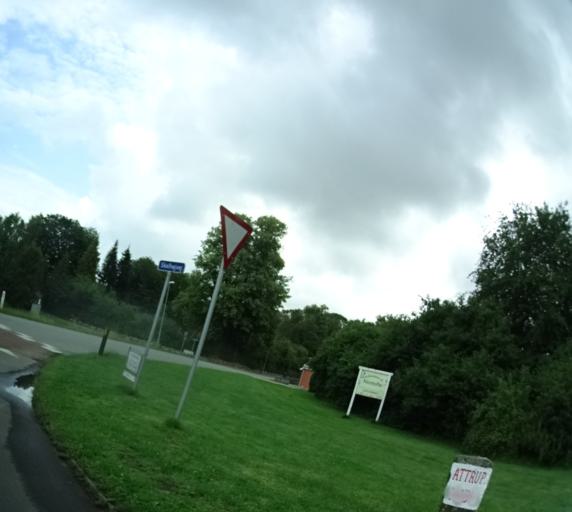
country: DK
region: Central Jutland
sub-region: Syddjurs Kommune
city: Ryomgard
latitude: 56.4080
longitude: 10.5584
